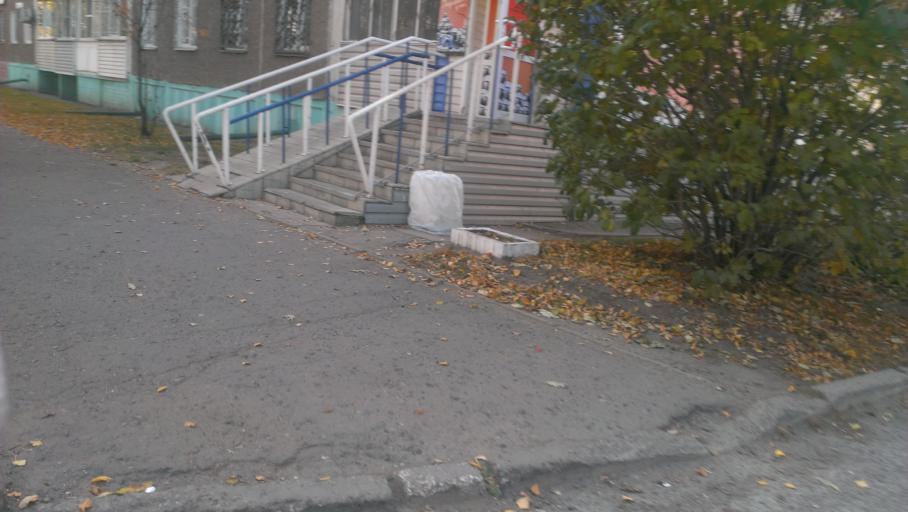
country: RU
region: Altai Krai
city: Novosilikatnyy
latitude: 53.3330
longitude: 83.6764
